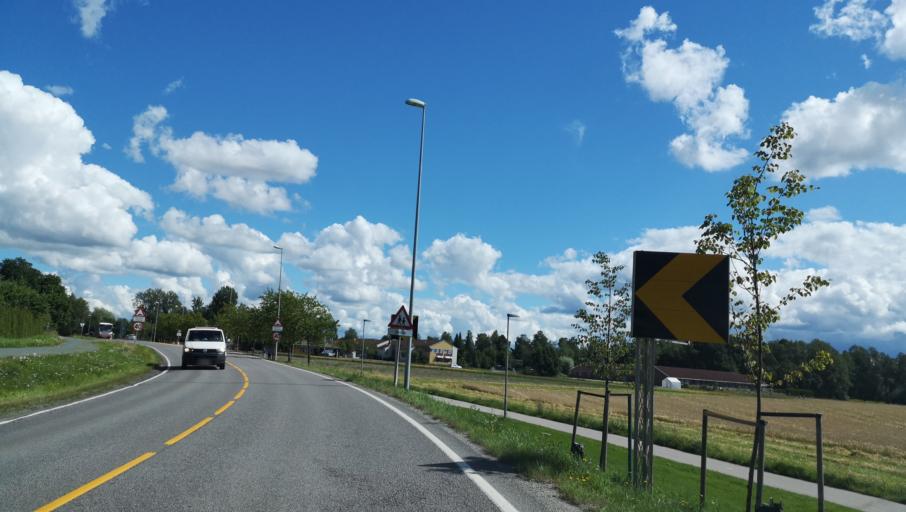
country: NO
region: Akershus
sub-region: As
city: As
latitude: 59.6642
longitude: 10.7815
